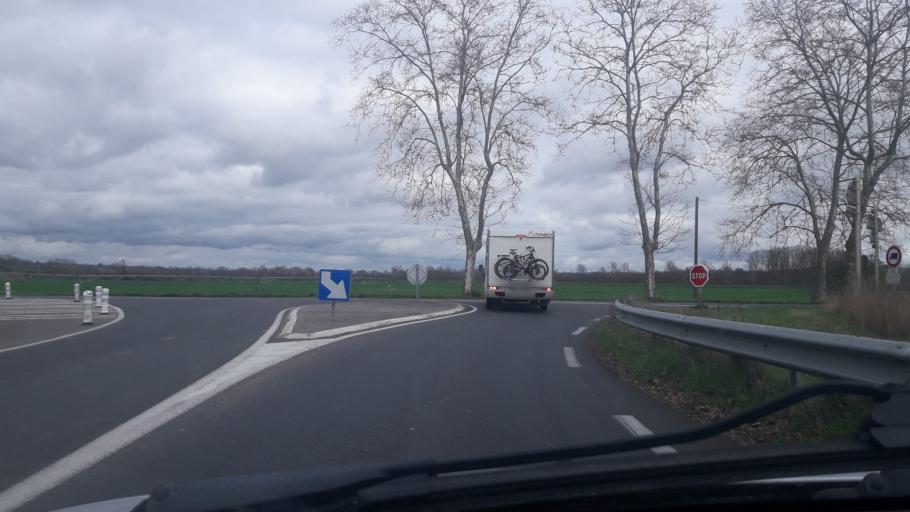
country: FR
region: Midi-Pyrenees
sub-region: Departement du Gers
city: Pujaudran
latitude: 43.6207
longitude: 1.0717
